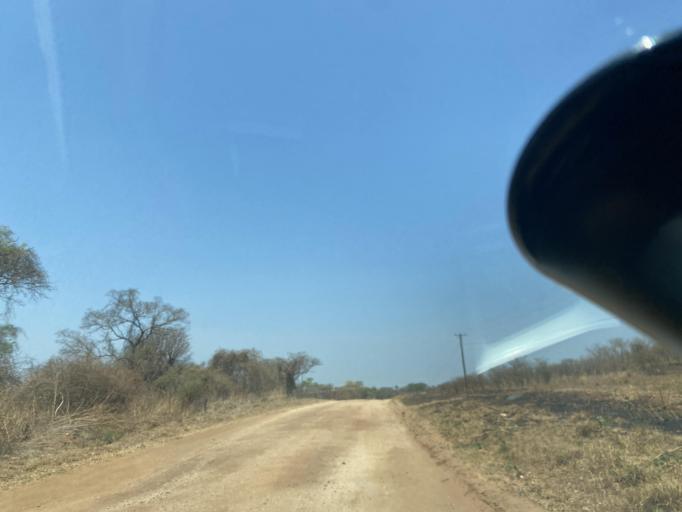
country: ZM
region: Lusaka
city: Lusaka
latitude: -15.5416
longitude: 28.0757
